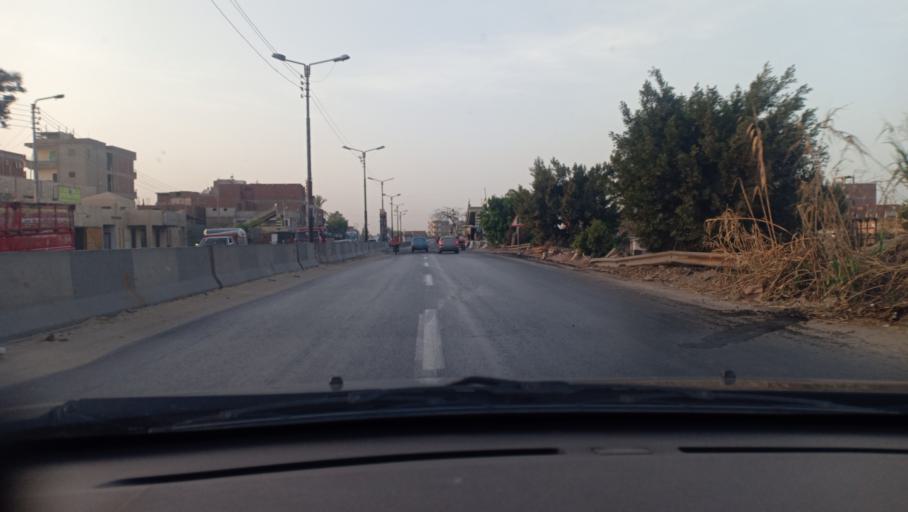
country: EG
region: Muhafazat al Gharbiyah
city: Zifta
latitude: 30.6699
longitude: 31.2858
